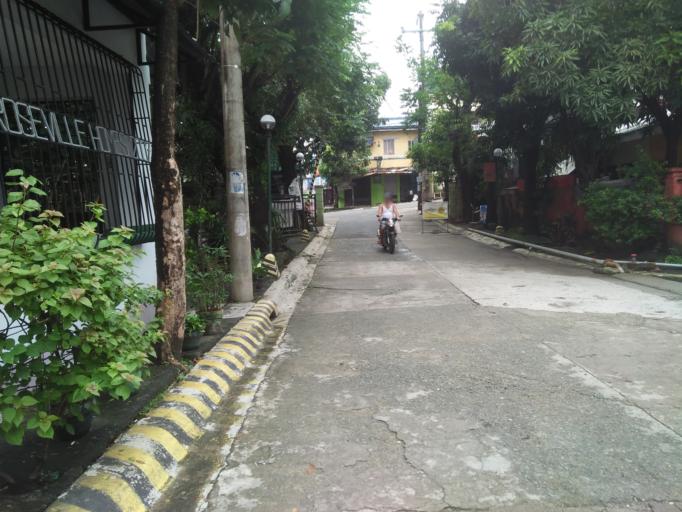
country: PH
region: Central Luzon
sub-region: Province of Bulacan
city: San Jose del Monte
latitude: 14.7492
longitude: 121.0637
